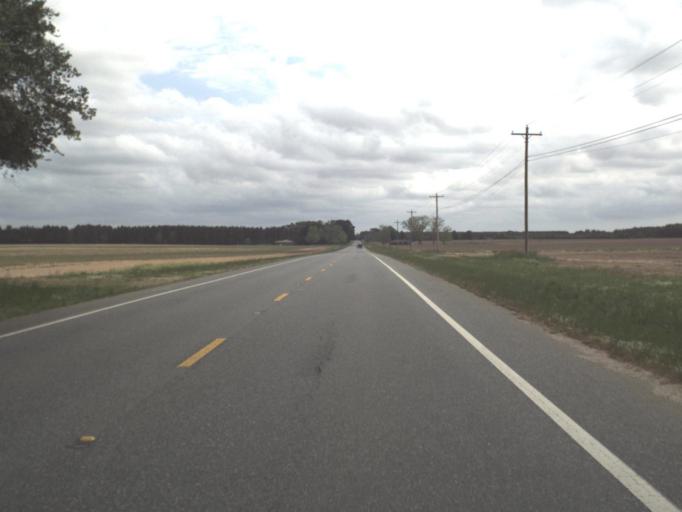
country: US
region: Florida
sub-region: Santa Rosa County
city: Point Baker
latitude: 30.8708
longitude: -87.0525
